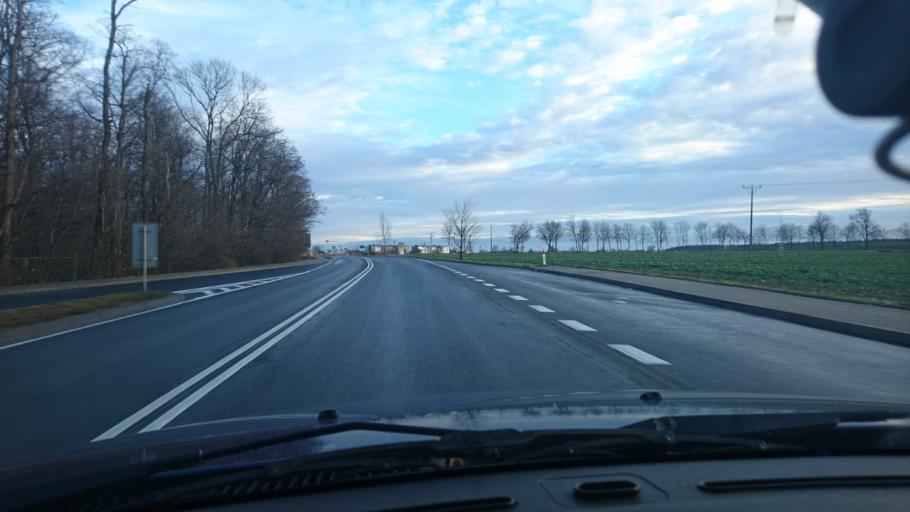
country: PL
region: Greater Poland Voivodeship
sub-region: Powiat kepinski
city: Slupia pod Kepnem
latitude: 51.2407
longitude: 18.0346
